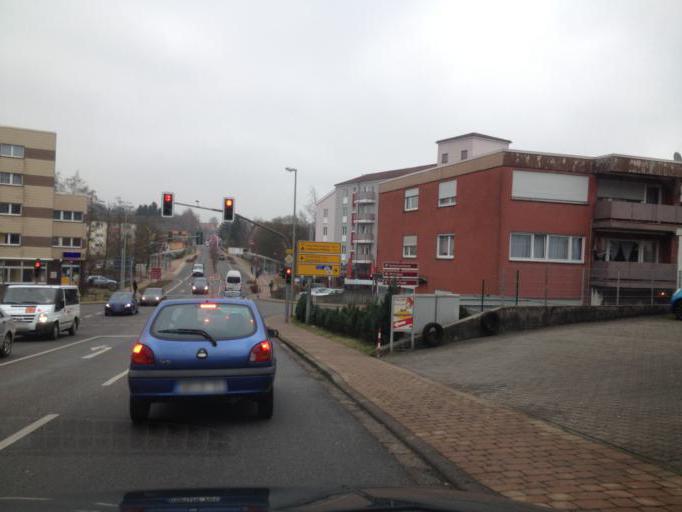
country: DE
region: Rheinland-Pfalz
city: Waldmohr
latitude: 49.3872
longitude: 7.3349
